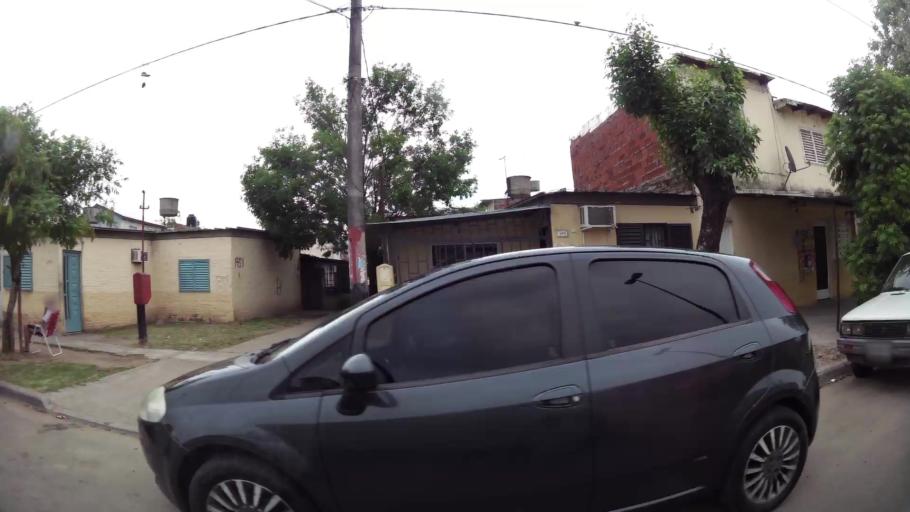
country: AR
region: Santa Fe
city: Gobernador Galvez
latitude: -33.0092
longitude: -60.6583
